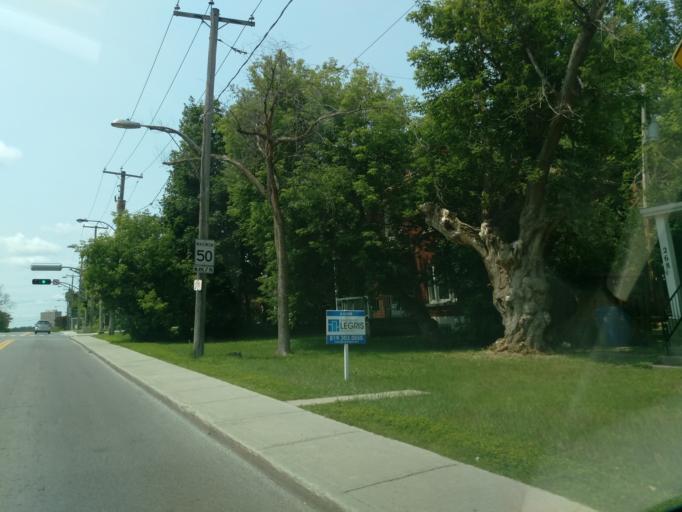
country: CA
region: Ontario
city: Ottawa
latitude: 45.4230
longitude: -75.7376
